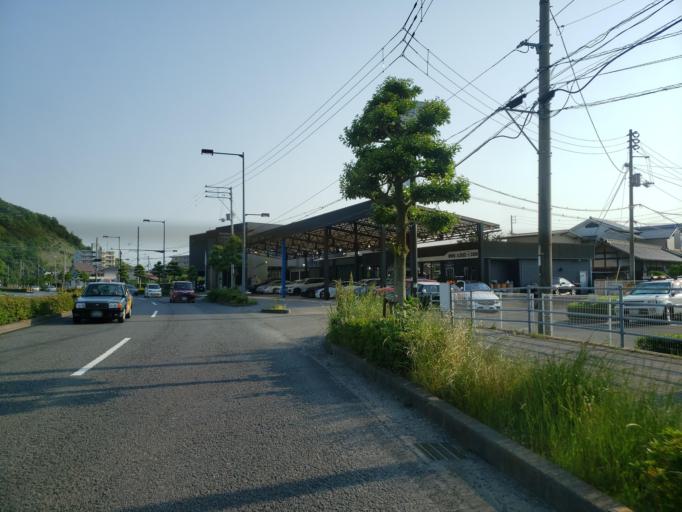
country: JP
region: Ehime
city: Masaki-cho
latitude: 33.8366
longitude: 132.7109
